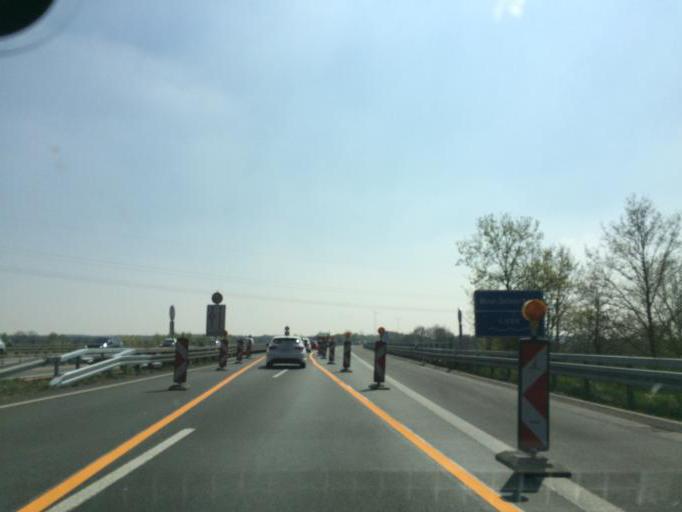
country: DE
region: North Rhine-Westphalia
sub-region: Regierungsbezirk Munster
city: Haltern
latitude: 51.7184
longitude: 7.1511
